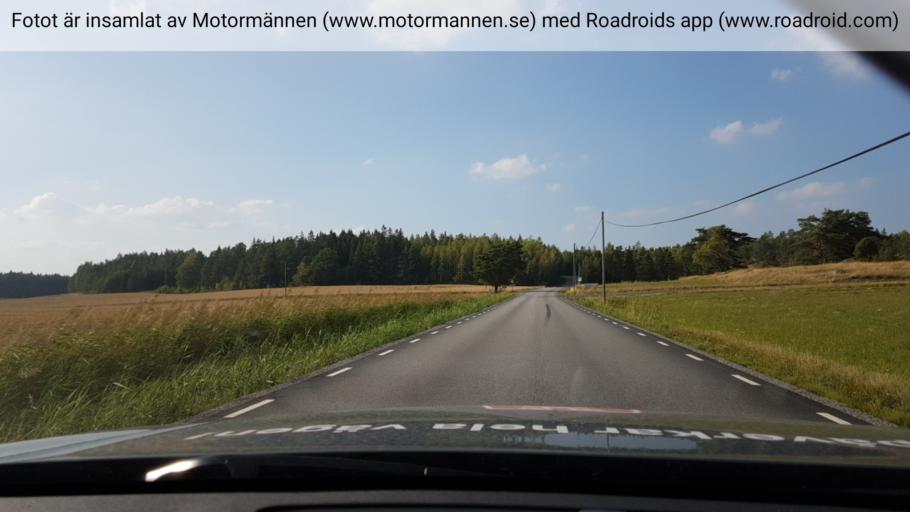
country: SE
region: Soedermanland
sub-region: Gnesta Kommun
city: Gnesta
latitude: 59.1136
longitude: 17.2219
